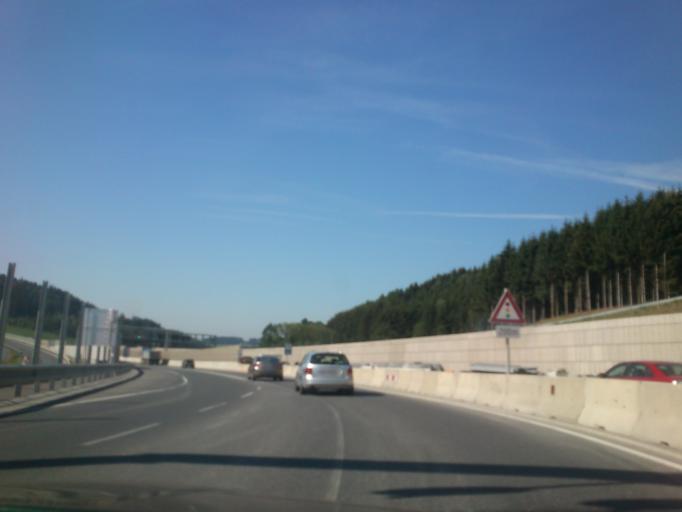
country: AT
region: Upper Austria
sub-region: Politischer Bezirk Freistadt
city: Freistadt
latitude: 48.4405
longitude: 14.4821
